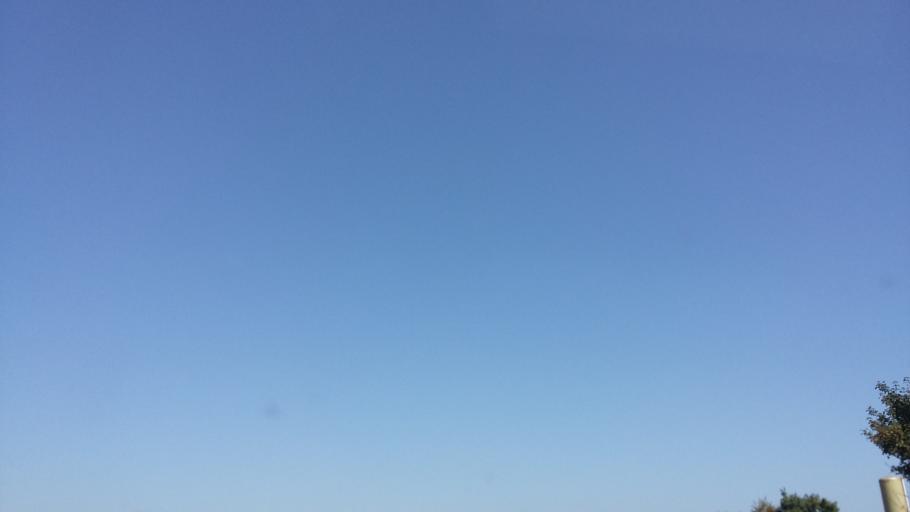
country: DE
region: Bavaria
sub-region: Swabia
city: Oberottmarshausen
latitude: 48.2246
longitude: 10.8663
